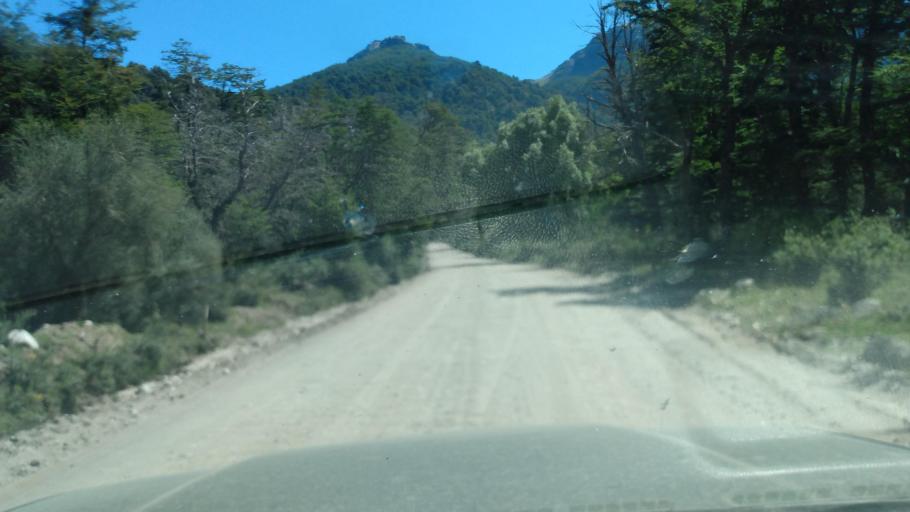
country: AR
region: Neuquen
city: Villa La Angostura
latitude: -40.6244
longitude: -71.5863
